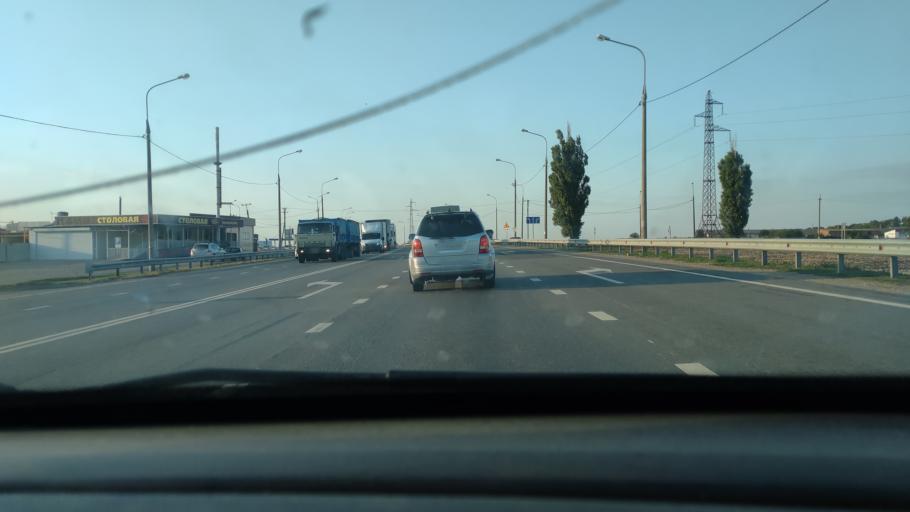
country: RU
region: Krasnodarskiy
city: Kanevskaya
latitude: 46.0756
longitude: 39.0147
